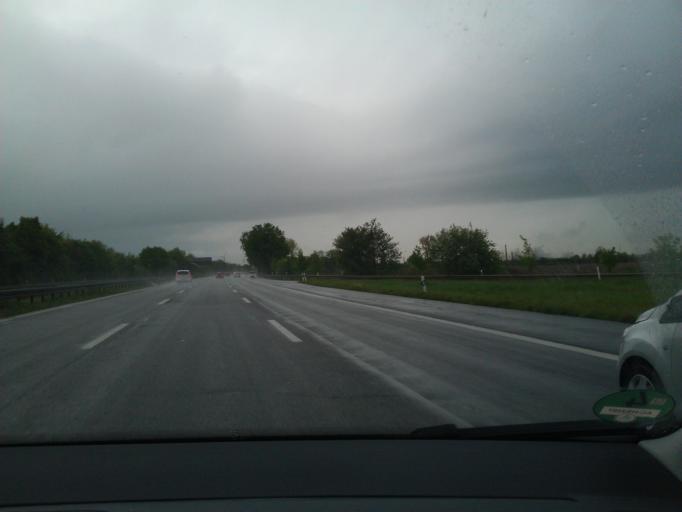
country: DE
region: North Rhine-Westphalia
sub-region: Regierungsbezirk Koln
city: Alfter
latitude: 50.7655
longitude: 7.0298
